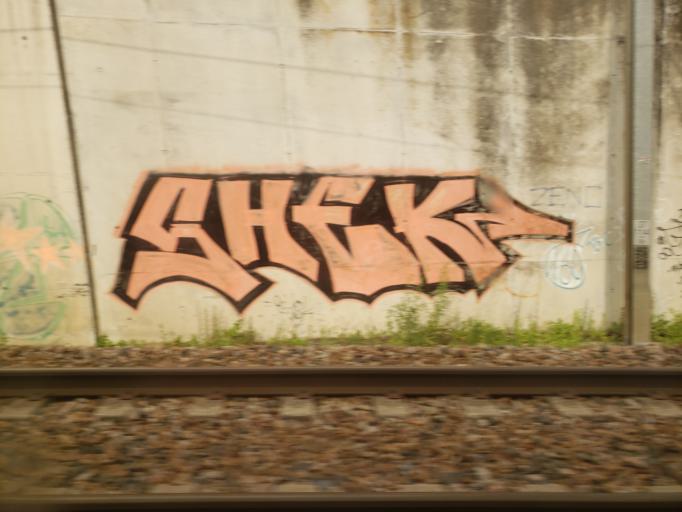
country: FR
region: Ile-de-France
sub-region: Departement de Seine-et-Marne
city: Serris
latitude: 48.8186
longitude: 2.7835
